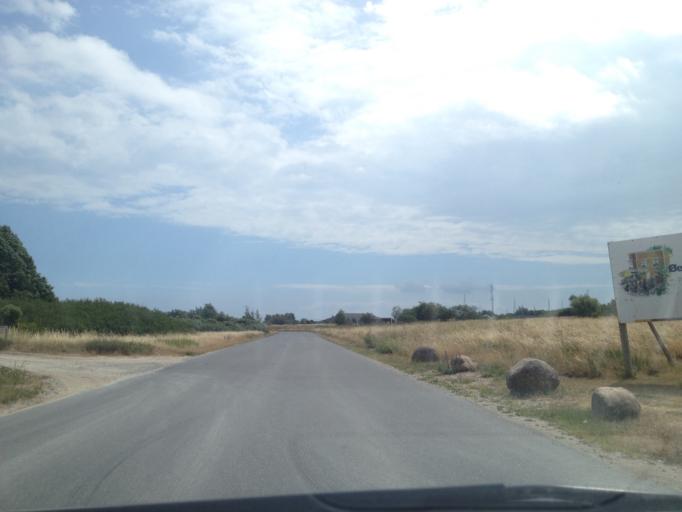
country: DK
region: Central Jutland
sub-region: Syddjurs Kommune
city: Ebeltoft
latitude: 56.1543
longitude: 10.6867
